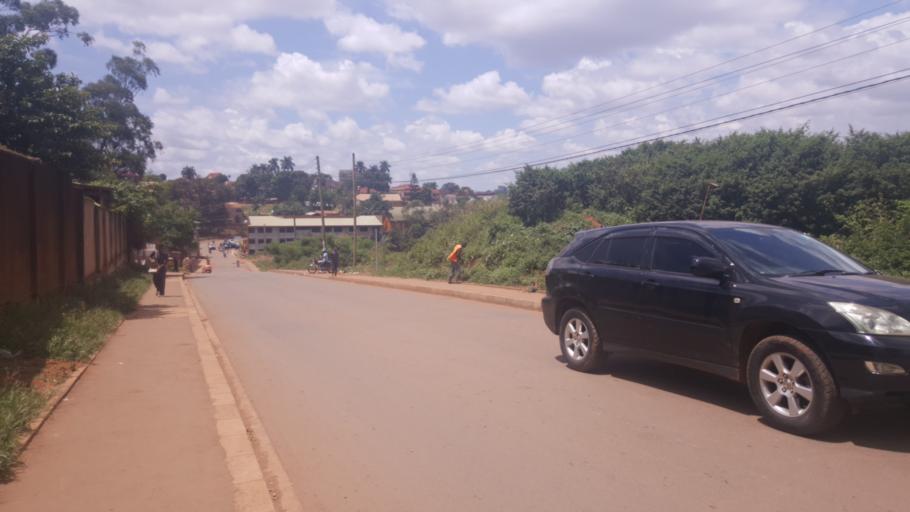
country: UG
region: Central Region
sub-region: Kampala District
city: Kampala
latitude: 0.3038
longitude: 32.5837
